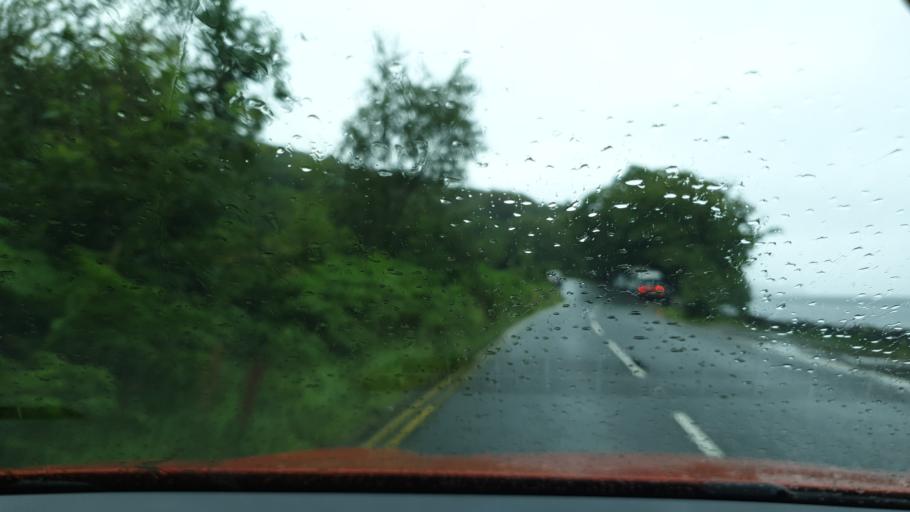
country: GB
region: England
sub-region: Cumbria
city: Ulverston
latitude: 54.3121
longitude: -3.0917
